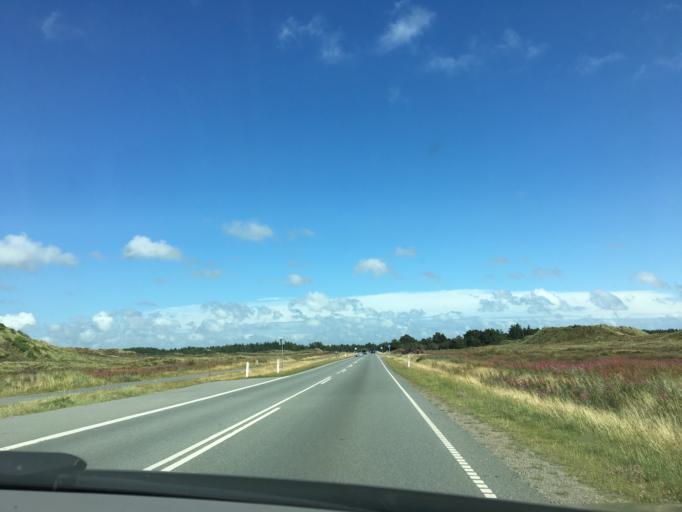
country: DK
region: South Denmark
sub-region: Varde Kommune
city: Oksbol
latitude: 55.7347
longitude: 8.1888
